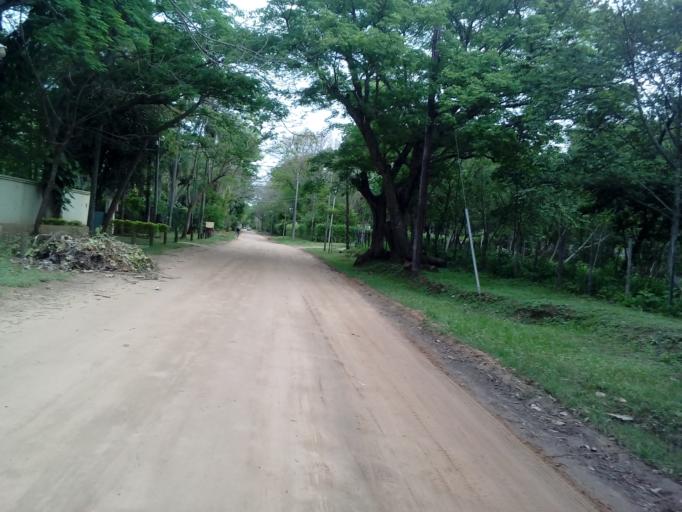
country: AR
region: Corrientes
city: San Luis del Palmar
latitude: -27.4599
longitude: -58.6608
